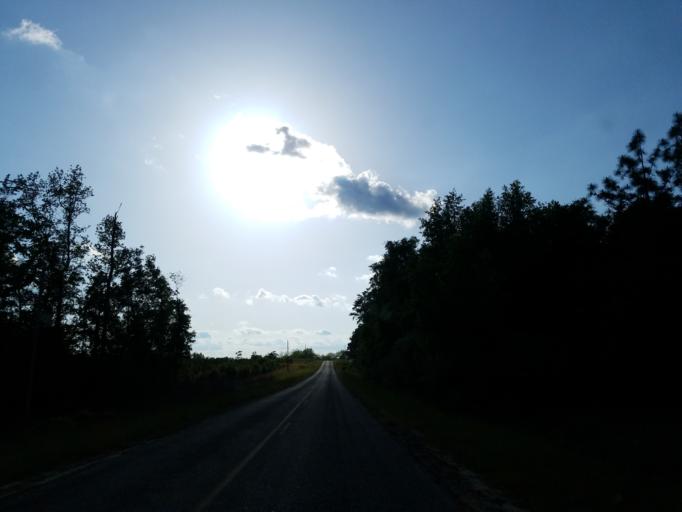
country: US
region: Georgia
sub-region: Turner County
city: Ashburn
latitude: 31.6086
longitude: -83.5918
